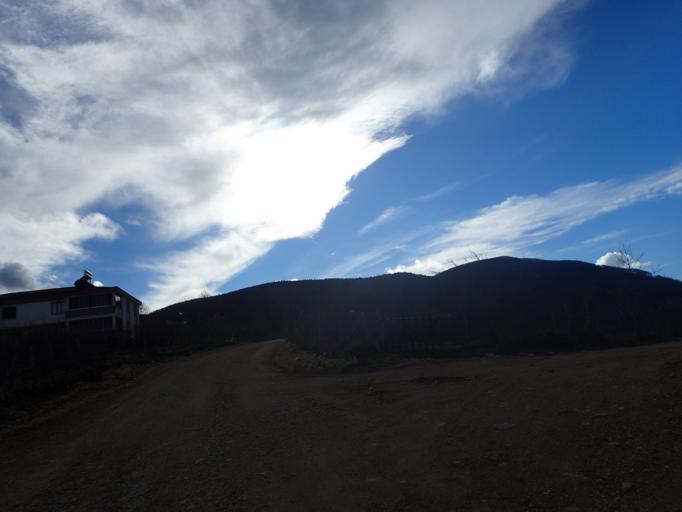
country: TR
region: Ordu
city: Kumru
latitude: 40.9296
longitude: 37.2503
